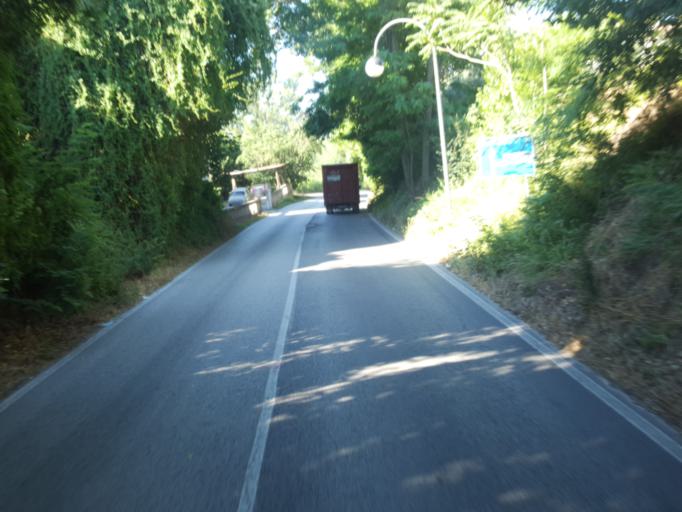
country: IT
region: The Marches
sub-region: Provincia di Pesaro e Urbino
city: Borgo Massano
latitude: 43.8133
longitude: 12.6636
